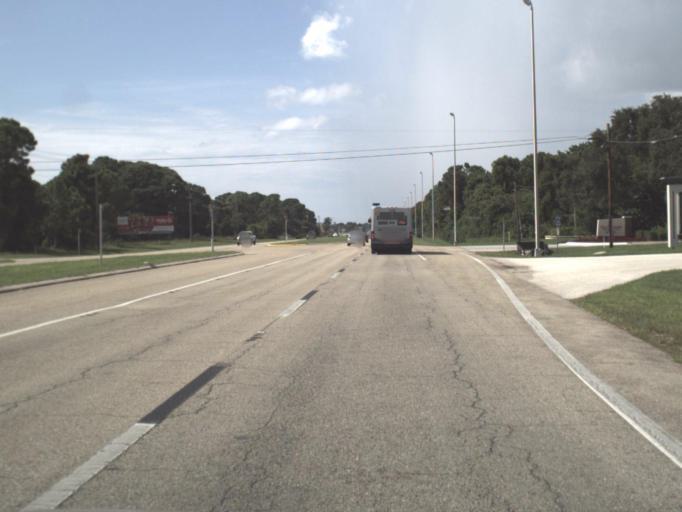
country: US
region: Florida
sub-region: Sarasota County
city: Vamo
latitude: 27.2363
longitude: -82.5009
